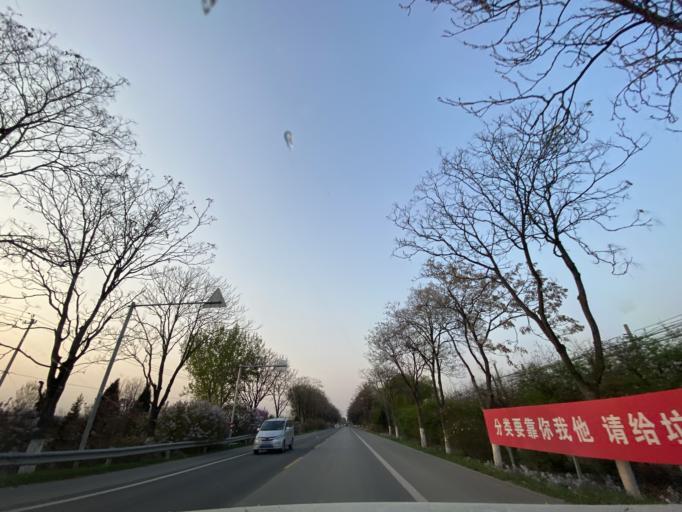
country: CN
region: Beijing
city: Weishanzhuang
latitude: 39.6101
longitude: 116.4096
